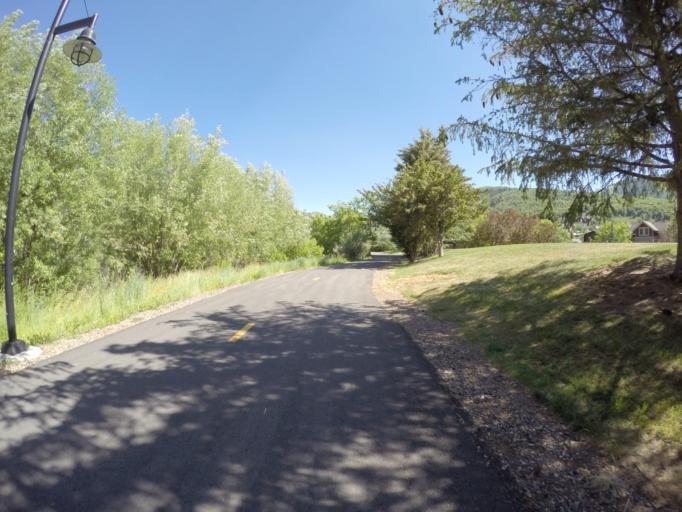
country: US
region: Utah
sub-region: Summit County
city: Park City
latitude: 40.6531
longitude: -111.5024
